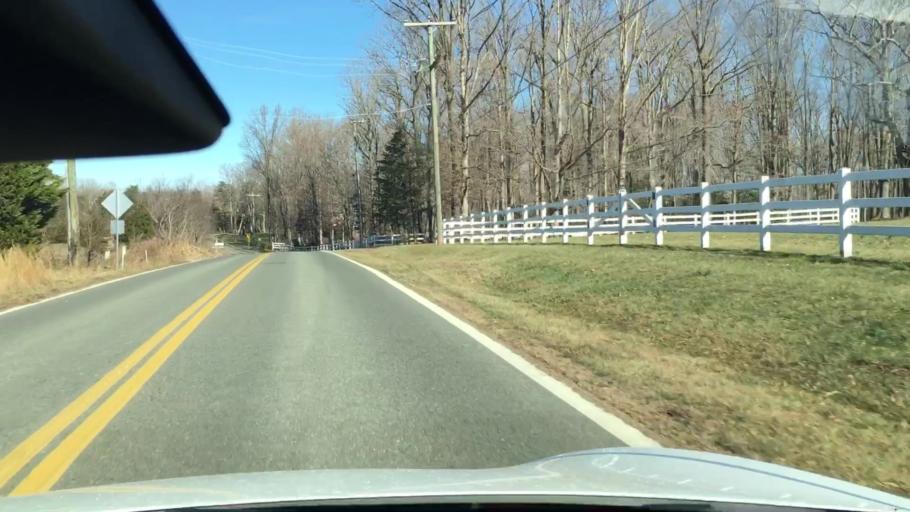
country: US
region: Virginia
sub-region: Powhatan County
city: Powhatan
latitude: 37.5535
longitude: -77.7967
